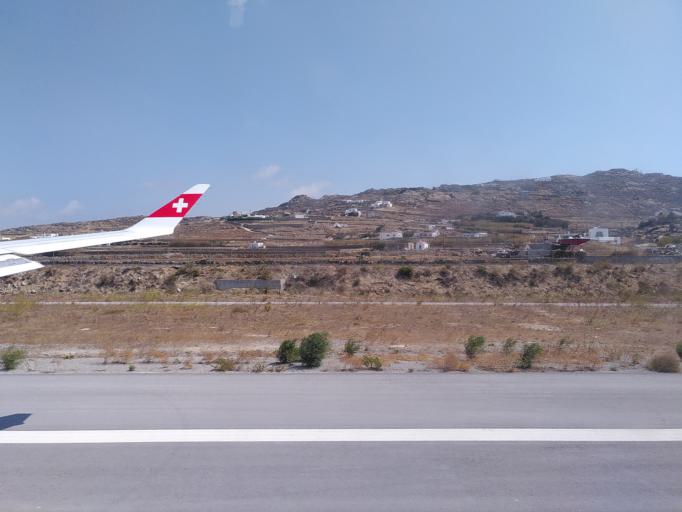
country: GR
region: South Aegean
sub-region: Nomos Kykladon
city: Mykonos
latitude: 37.4343
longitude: 25.3487
